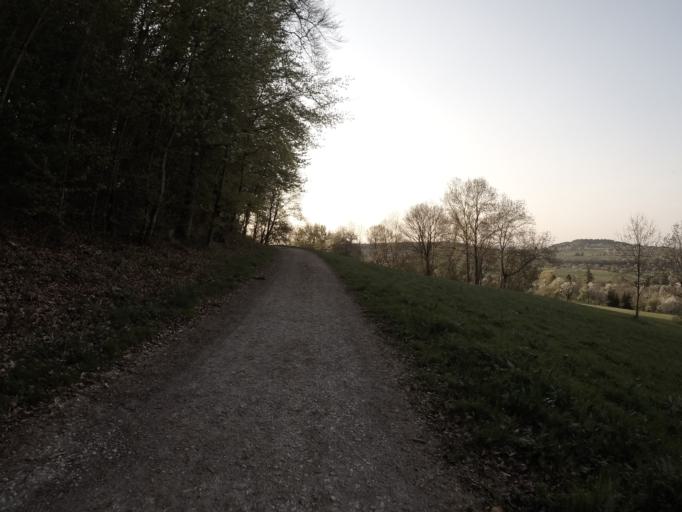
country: DE
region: Baden-Wuerttemberg
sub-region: Tuebingen Region
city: Pfullingen
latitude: 48.4426
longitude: 9.2069
